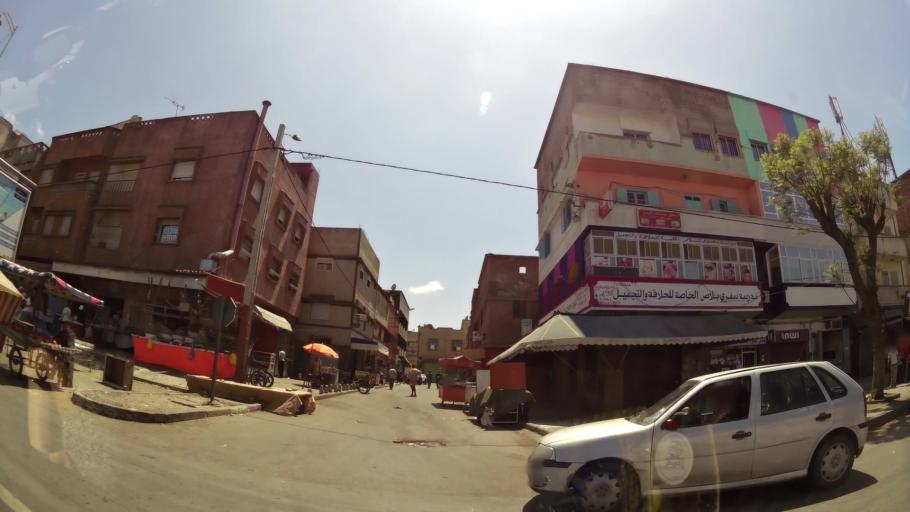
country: MA
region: Gharb-Chrarda-Beni Hssen
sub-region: Kenitra Province
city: Kenitra
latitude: 34.2450
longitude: -6.5518
